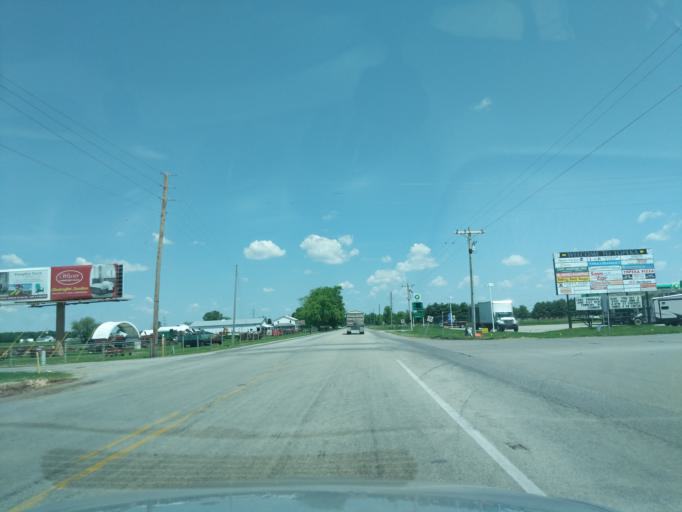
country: US
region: Indiana
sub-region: LaGrange County
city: Topeka
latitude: 41.5387
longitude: -85.5779
